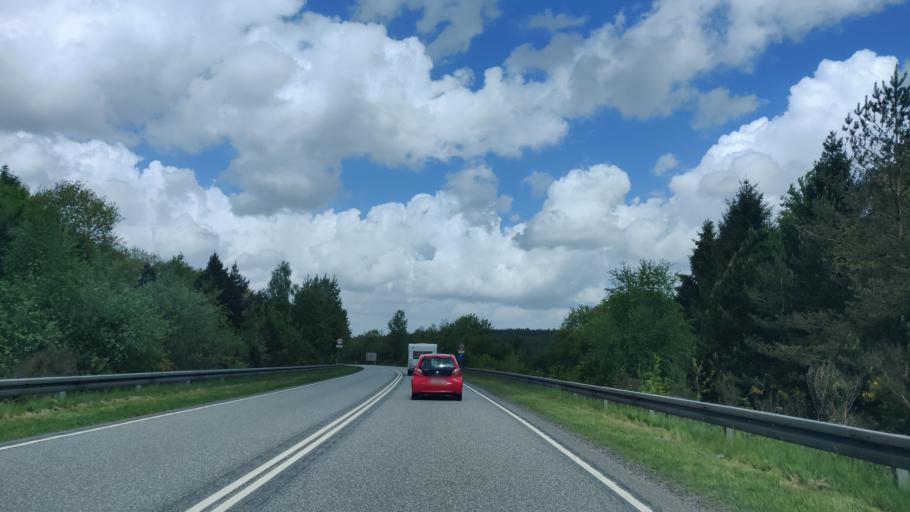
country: DK
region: Central Jutland
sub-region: Hedensted Kommune
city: Torring
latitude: 55.9642
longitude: 9.4056
